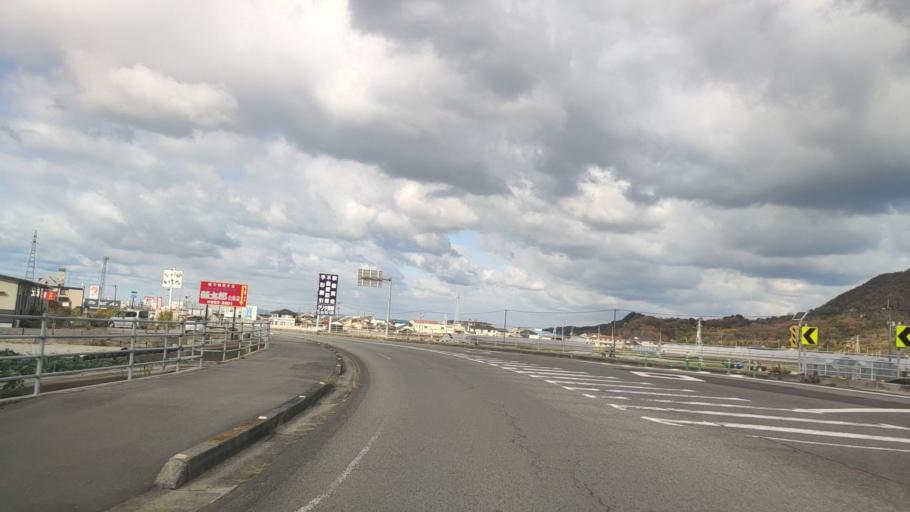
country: JP
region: Ehime
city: Hojo
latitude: 33.9804
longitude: 132.7854
